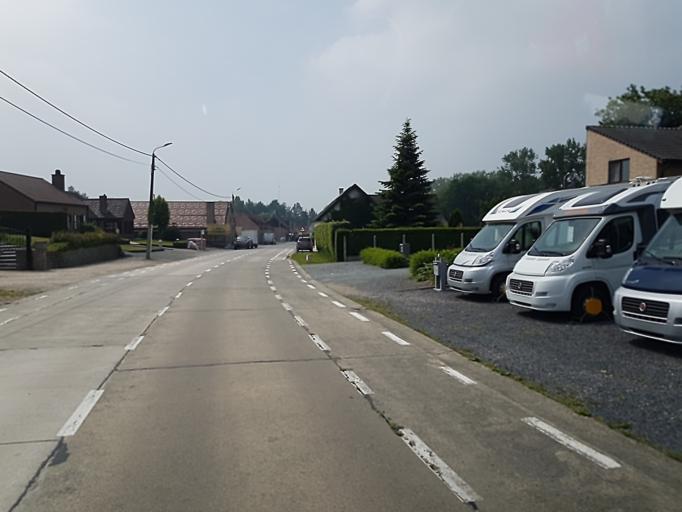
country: BE
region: Flanders
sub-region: Provincie Oost-Vlaanderen
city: Sint-Maria-Lierde
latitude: 50.8176
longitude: 3.8833
